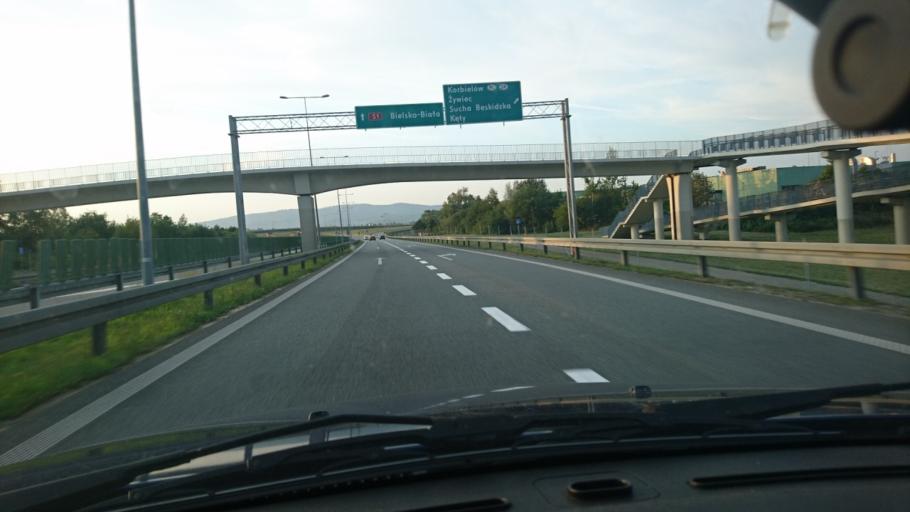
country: PL
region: Silesian Voivodeship
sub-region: Powiat zywiecki
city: Pietrzykowice
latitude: 49.6768
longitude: 19.1690
